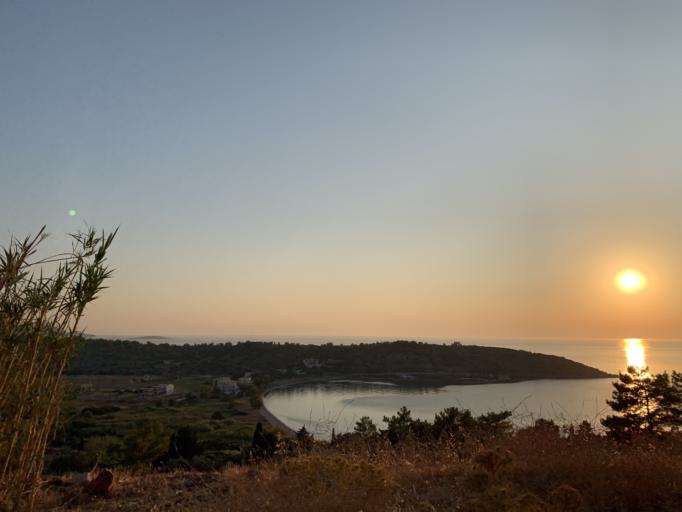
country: GR
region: North Aegean
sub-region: Chios
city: Thymiana
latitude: 38.3422
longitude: 25.9989
